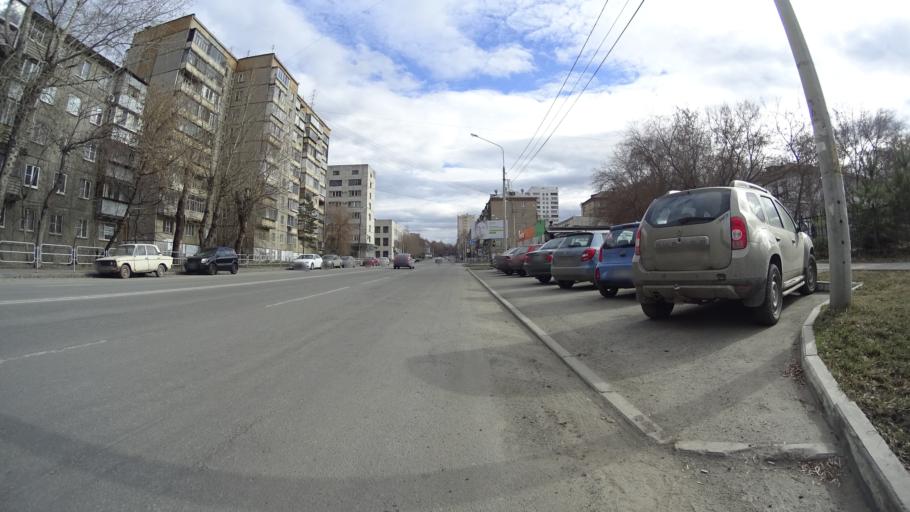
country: RU
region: Chelyabinsk
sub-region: Gorod Chelyabinsk
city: Chelyabinsk
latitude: 55.1633
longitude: 61.3861
